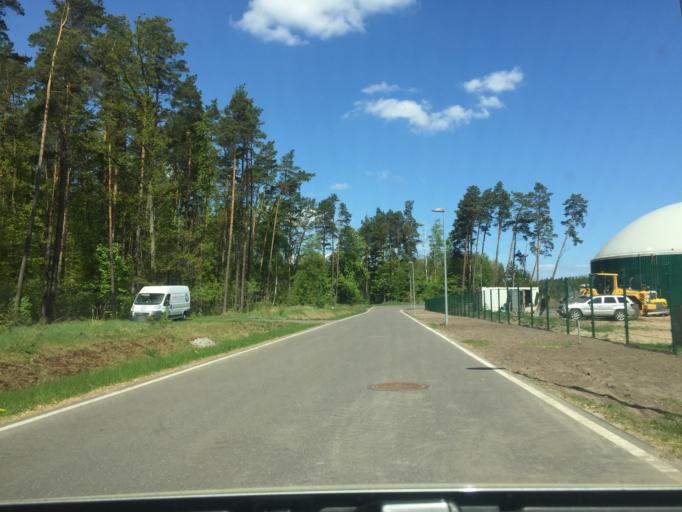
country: DE
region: Mecklenburg-Vorpommern
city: Torgelow
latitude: 53.6366
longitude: 13.9866
